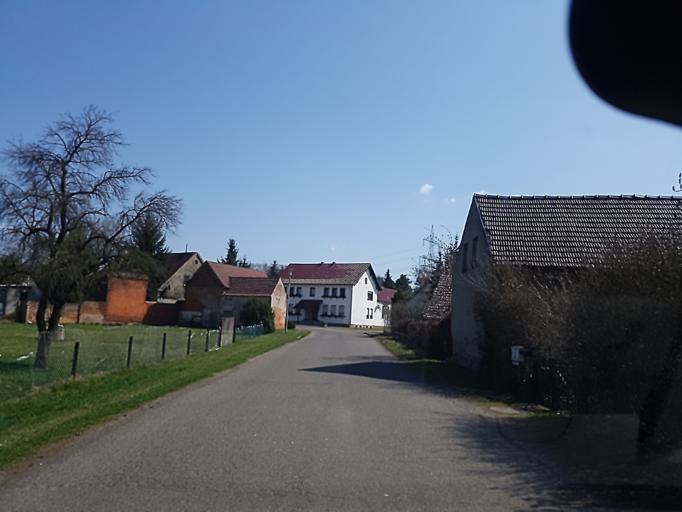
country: DE
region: Brandenburg
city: Schonborn
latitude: 51.5603
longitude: 13.4833
